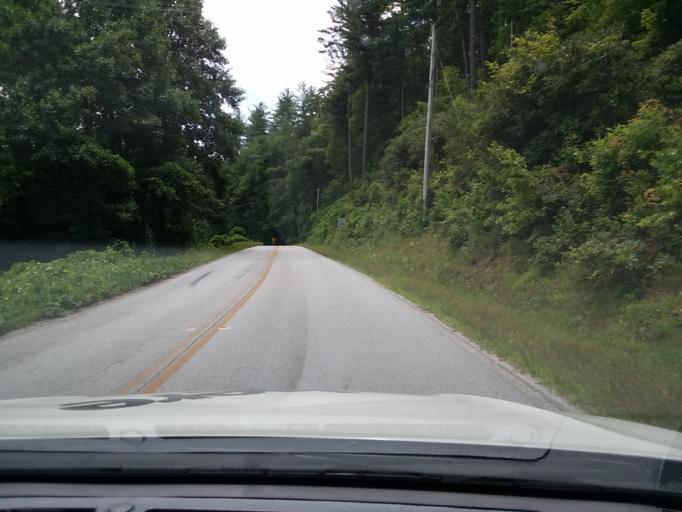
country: US
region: Georgia
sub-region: Rabun County
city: Mountain City
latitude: 34.9938
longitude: -83.1953
